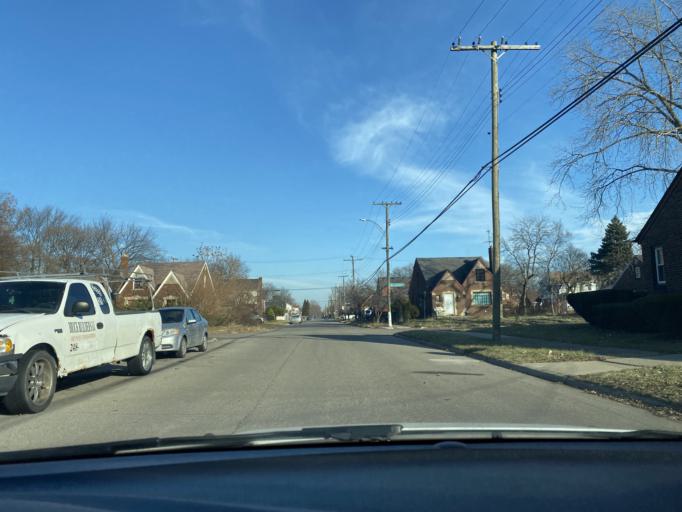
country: US
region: Michigan
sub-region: Wayne County
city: Grosse Pointe Park
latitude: 42.4052
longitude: -82.9546
